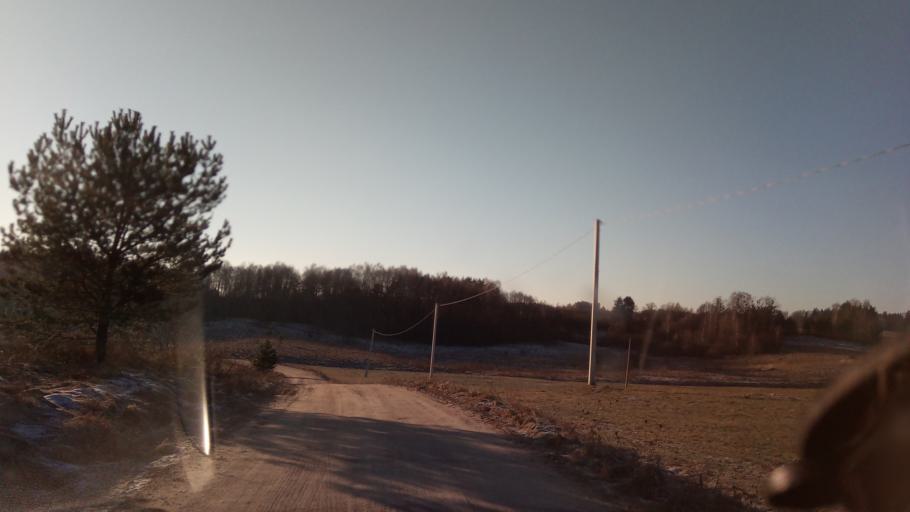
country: LT
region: Alytaus apskritis
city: Druskininkai
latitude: 54.1065
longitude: 24.0120
